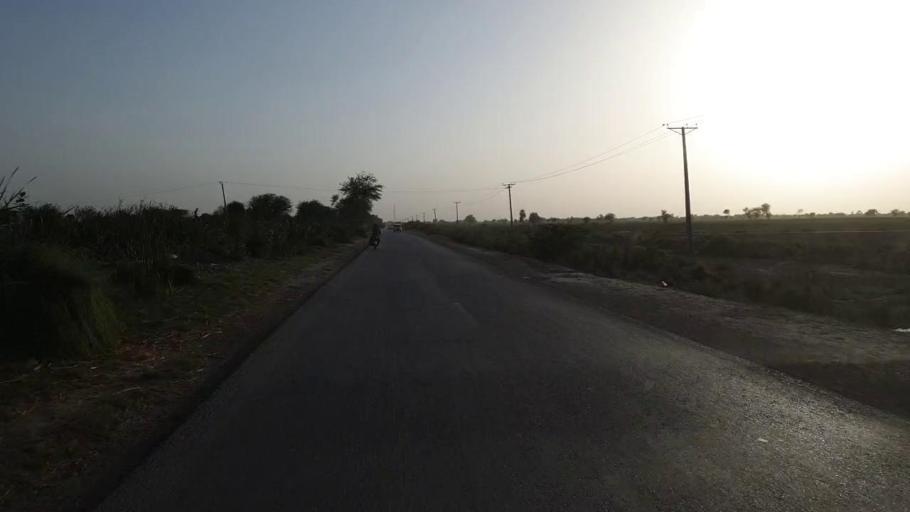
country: PK
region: Sindh
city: Jam Sahib
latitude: 26.2736
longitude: 68.5481
